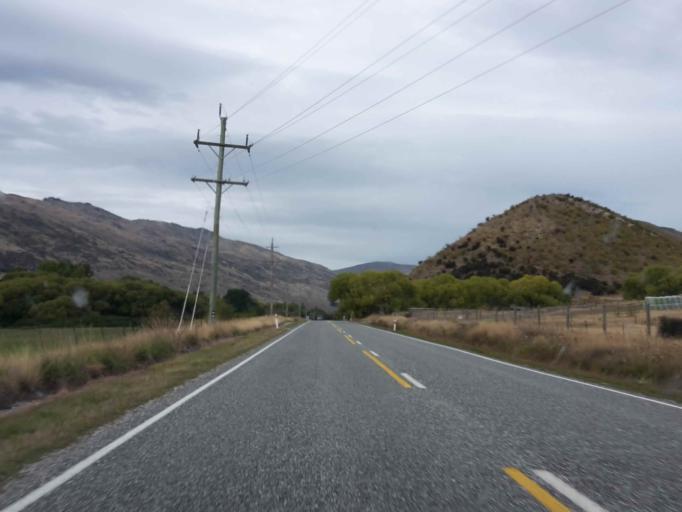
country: NZ
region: Otago
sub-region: Queenstown-Lakes District
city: Wanaka
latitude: -44.8037
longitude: 169.0697
